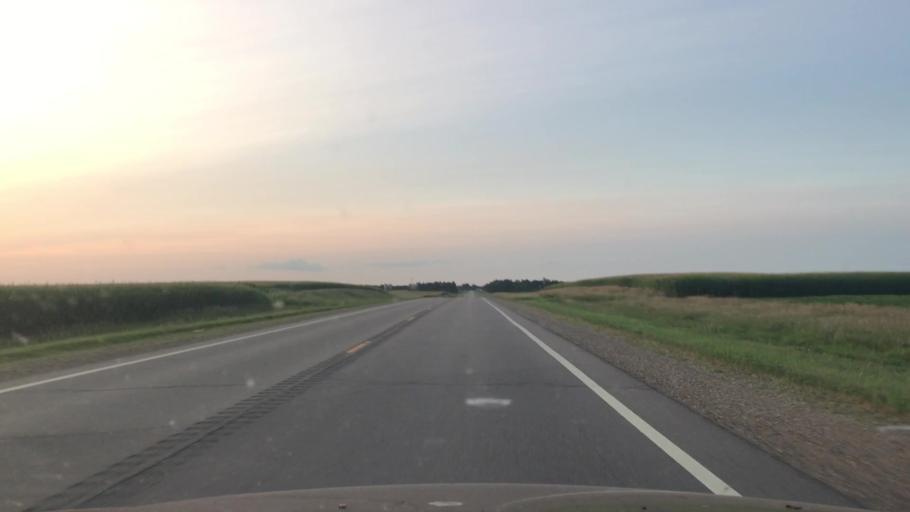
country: US
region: Minnesota
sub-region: Redwood County
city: Redwood Falls
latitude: 44.5062
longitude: -95.1178
